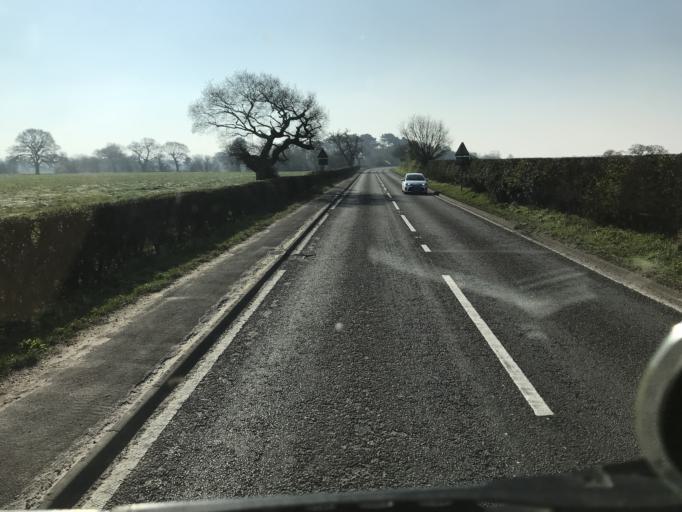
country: GB
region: England
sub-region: Cheshire West and Chester
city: Waverton
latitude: 53.1596
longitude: -2.8141
